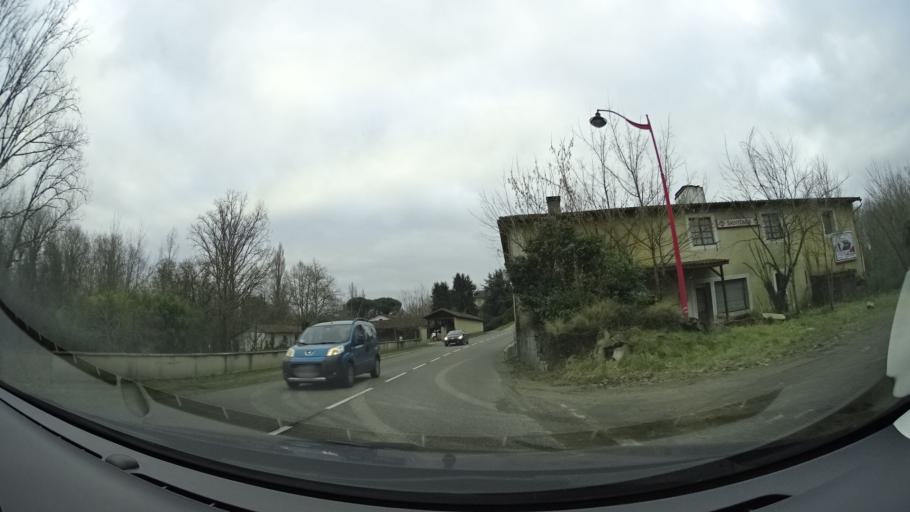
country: FR
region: Aquitaine
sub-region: Departement des Landes
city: Sarbazan
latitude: 43.9838
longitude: -0.2284
